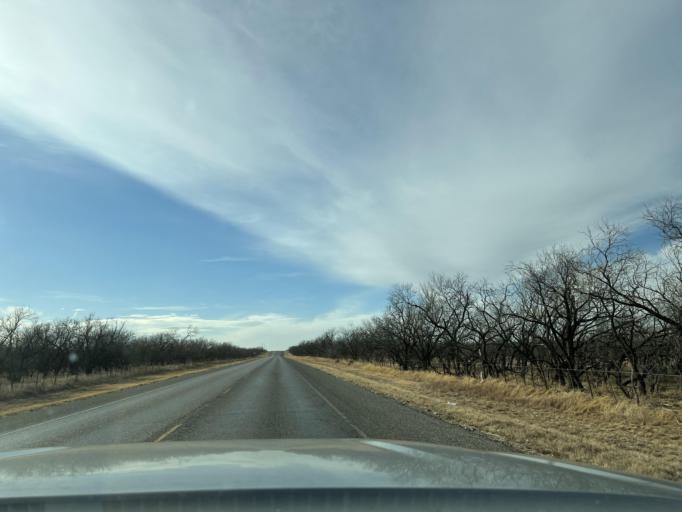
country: US
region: Texas
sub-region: Fisher County
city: Rotan
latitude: 32.7397
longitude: -100.5193
